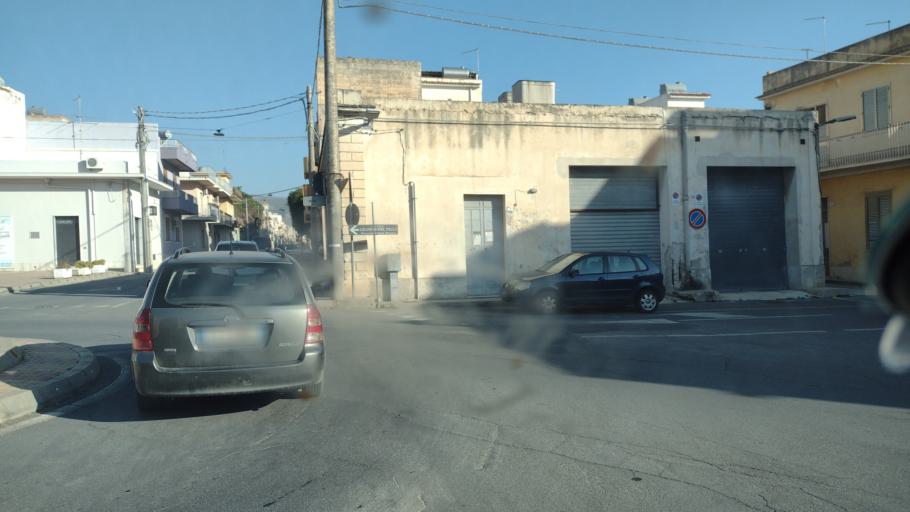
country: IT
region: Sicily
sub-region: Provincia di Siracusa
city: Avola
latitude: 36.9033
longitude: 15.1372
